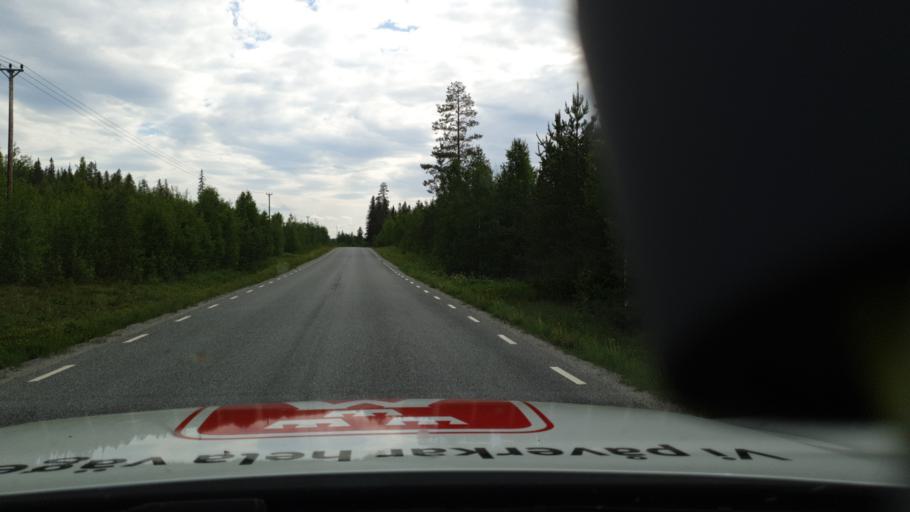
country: SE
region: Jaemtland
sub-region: Braecke Kommun
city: Braecke
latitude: 63.1320
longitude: 15.5086
